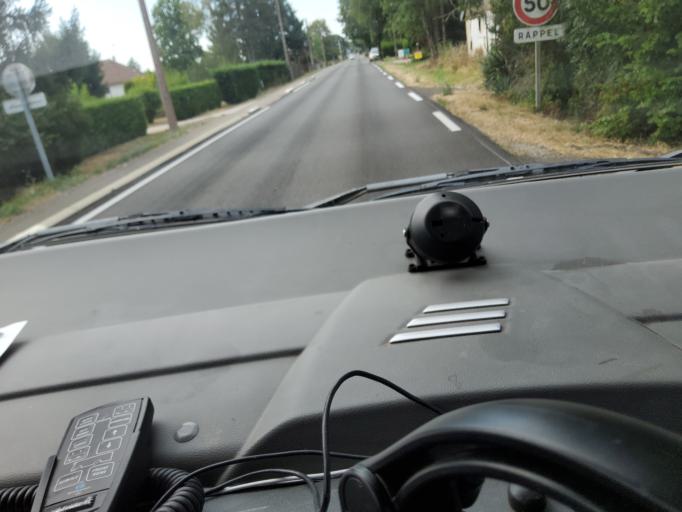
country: FR
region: Franche-Comte
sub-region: Departement du Jura
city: Chaussin
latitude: 46.9466
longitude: 5.5025
